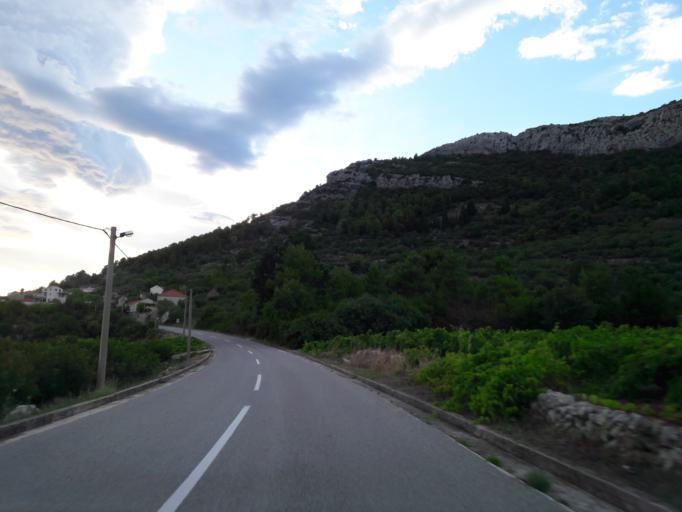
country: HR
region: Dubrovacko-Neretvanska
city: Ston
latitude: 42.8472
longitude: 17.6296
